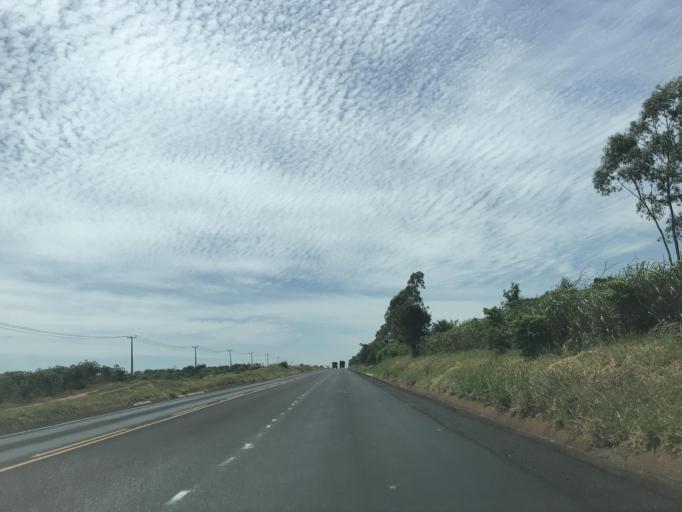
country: BR
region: Parana
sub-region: Paranavai
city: Paranavai
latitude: -23.0023
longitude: -52.5572
